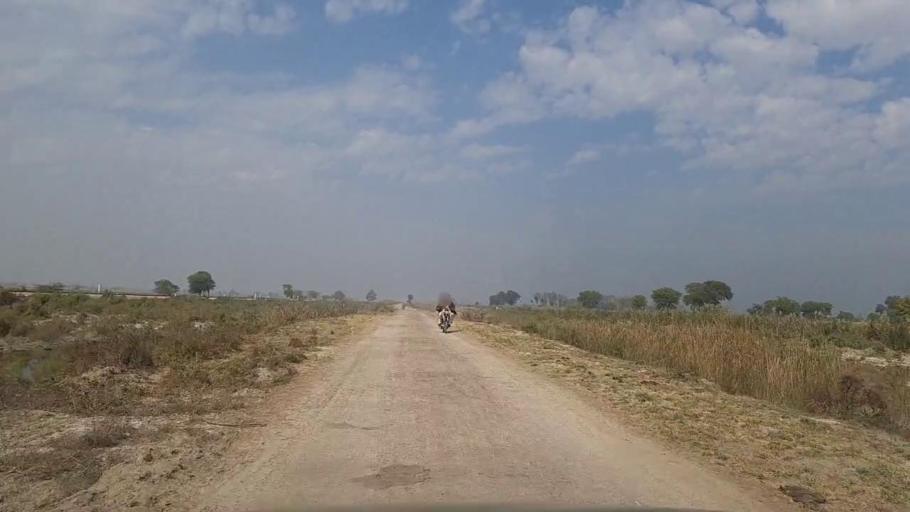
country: PK
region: Sindh
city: Daur
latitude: 26.3935
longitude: 68.3491
